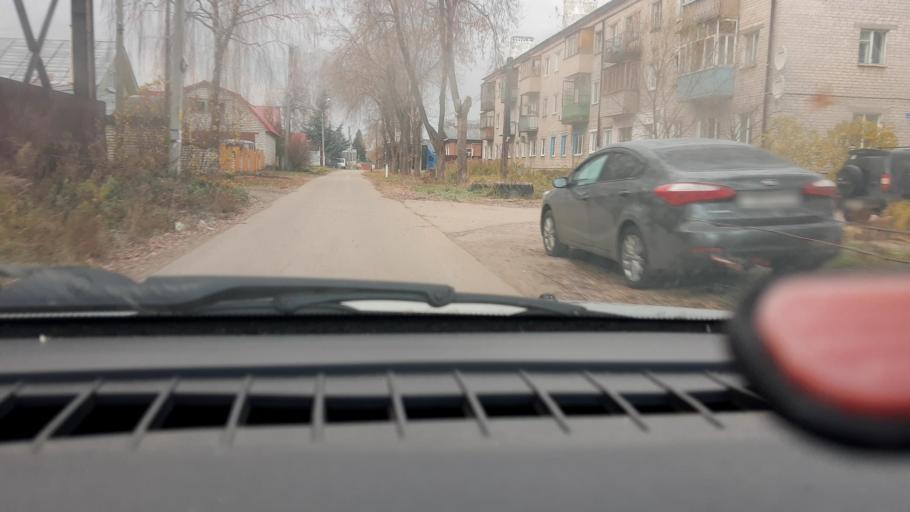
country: RU
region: Nizjnij Novgorod
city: Afonino
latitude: 56.2056
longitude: 44.1095
